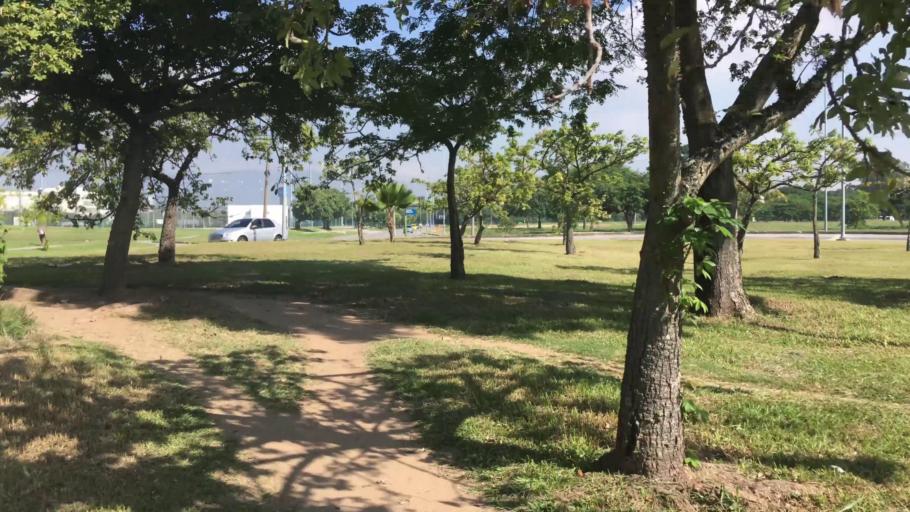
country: BR
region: Rio de Janeiro
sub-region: Rio De Janeiro
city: Rio de Janeiro
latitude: -22.8435
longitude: -43.2349
